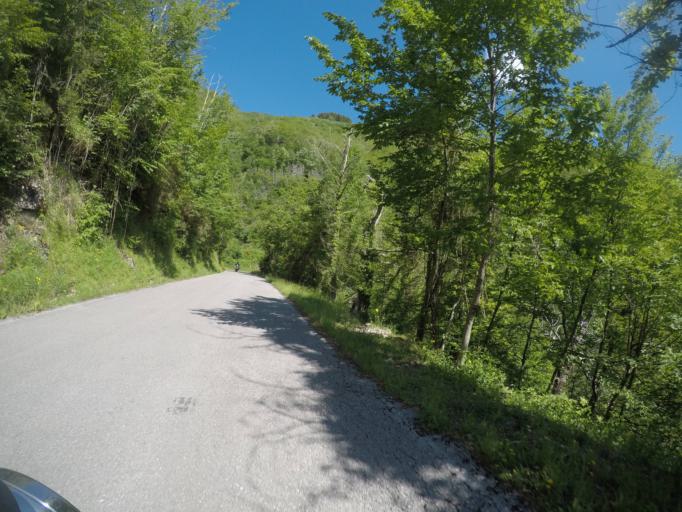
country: IT
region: Tuscany
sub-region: Provincia di Lucca
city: Careggine
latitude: 44.0743
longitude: 10.3308
